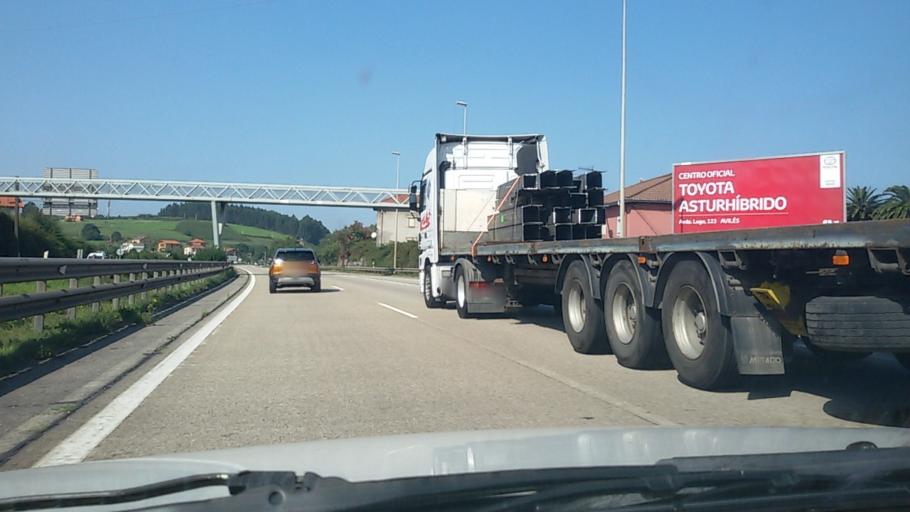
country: ES
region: Asturias
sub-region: Province of Asturias
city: Corvera de Asturias
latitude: 43.5502
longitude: -5.8732
